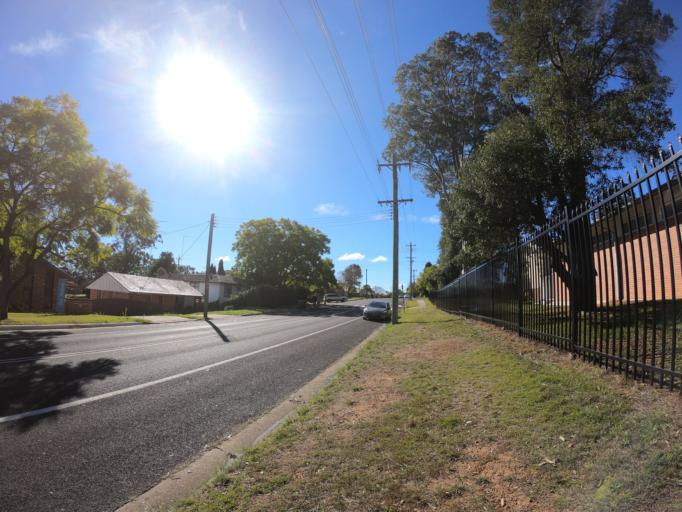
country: AU
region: New South Wales
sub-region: Hawkesbury
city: South Windsor
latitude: -33.6175
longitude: 150.8041
